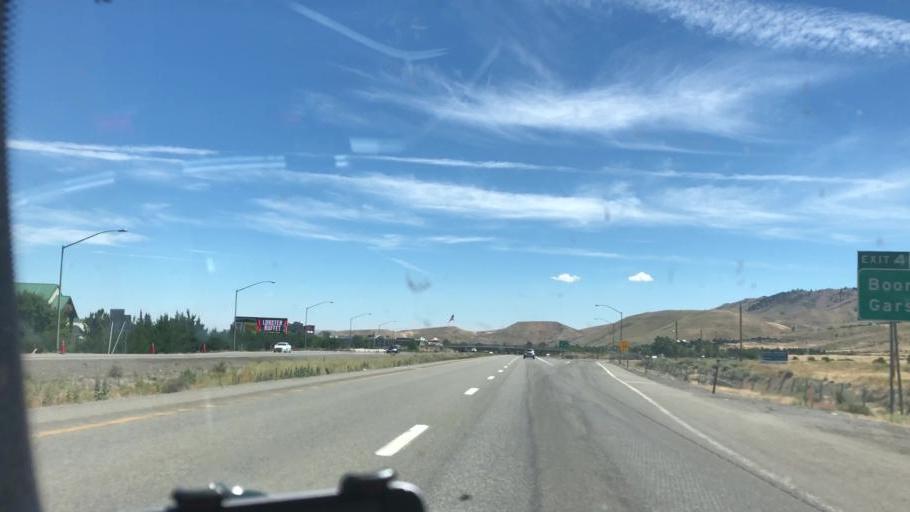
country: US
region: Nevada
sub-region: Washoe County
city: Verdi
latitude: 39.5123
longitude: -119.9709
